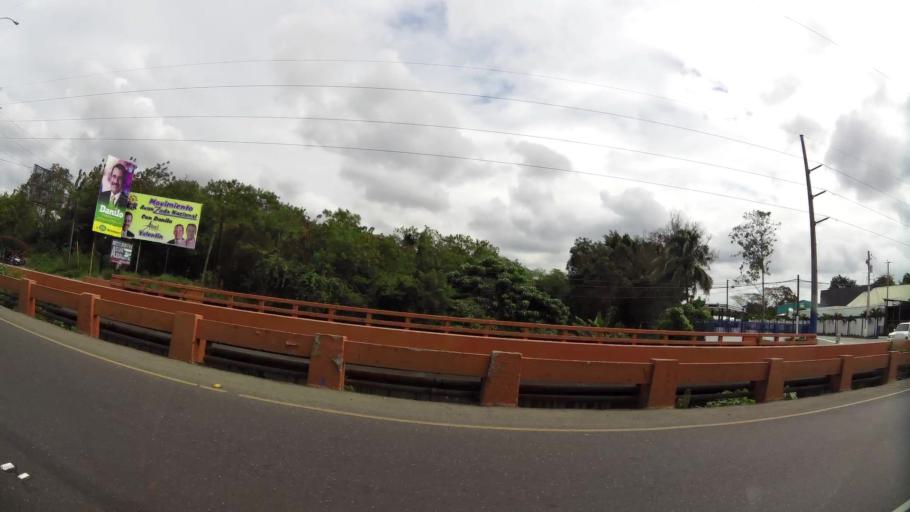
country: DO
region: Santiago
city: Santiago de los Caballeros
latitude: 19.4419
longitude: -70.6688
